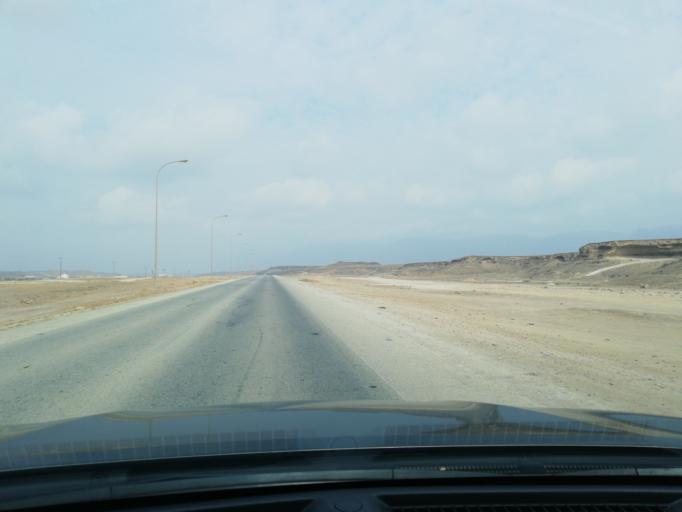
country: OM
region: Zufar
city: Salalah
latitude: 16.9545
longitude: 53.9168
